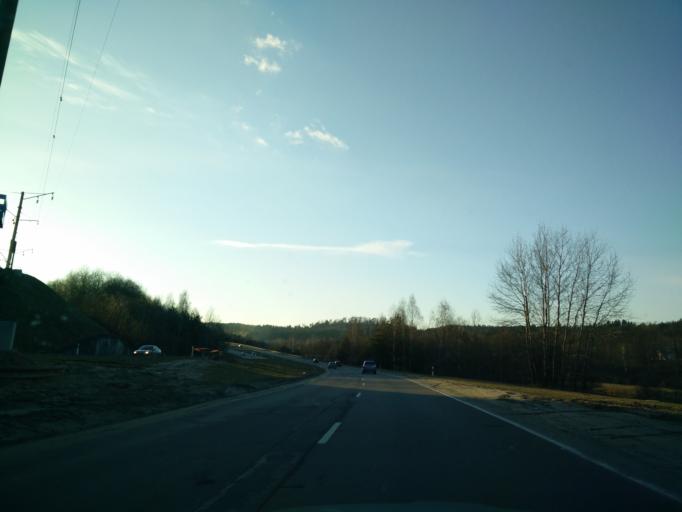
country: LT
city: Skaidiskes
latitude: 54.6927
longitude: 25.3894
